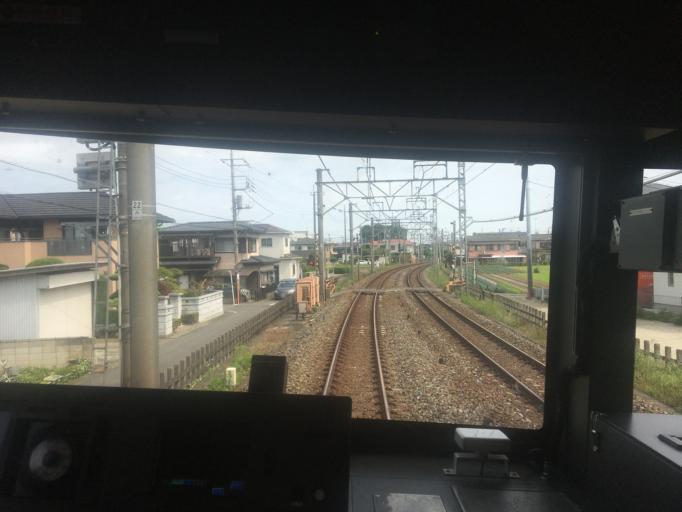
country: JP
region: Saitama
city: Sakado
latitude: 35.9597
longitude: 139.3890
